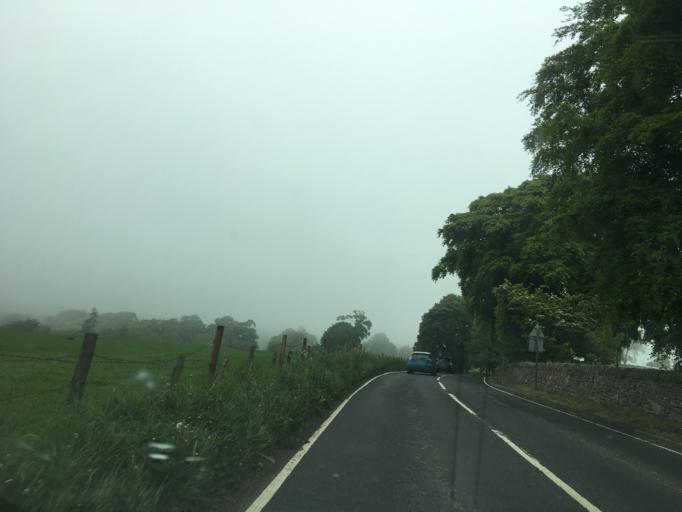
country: GB
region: Scotland
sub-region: Midlothian
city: Penicuik
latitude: 55.8354
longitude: -3.2003
